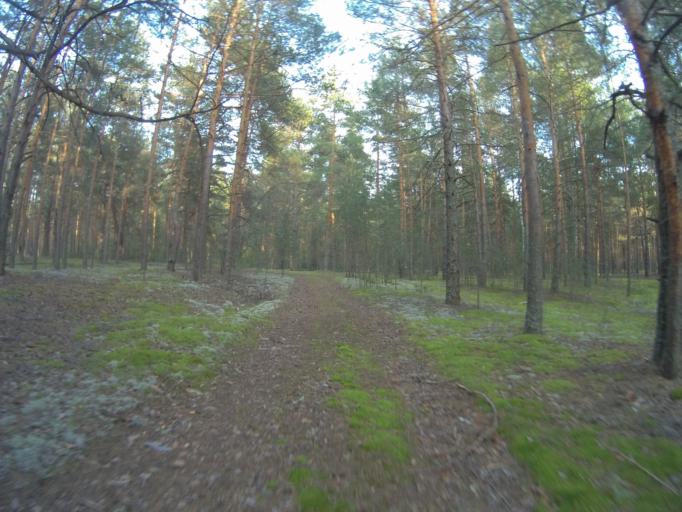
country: RU
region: Vladimir
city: Kommunar
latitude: 56.0803
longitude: 40.4359
